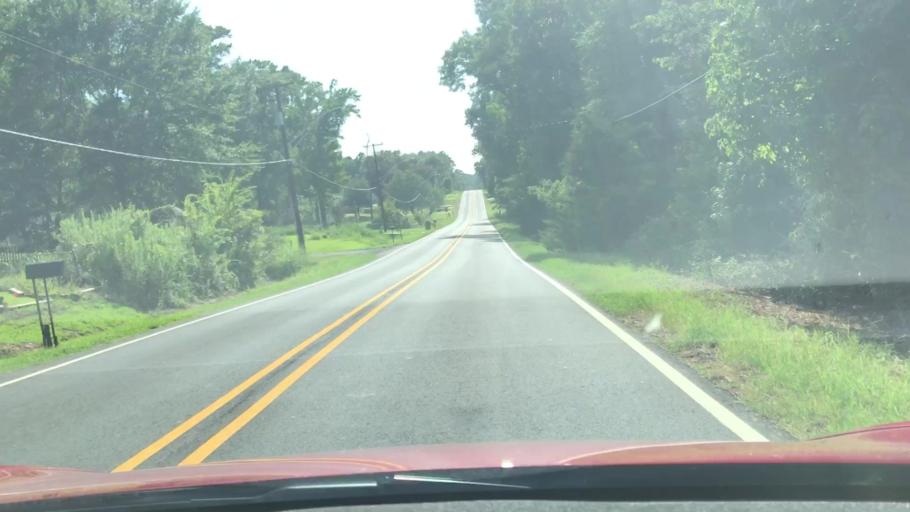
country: US
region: Louisiana
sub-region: Bossier Parish
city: Bossier City
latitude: 32.3910
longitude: -93.7560
